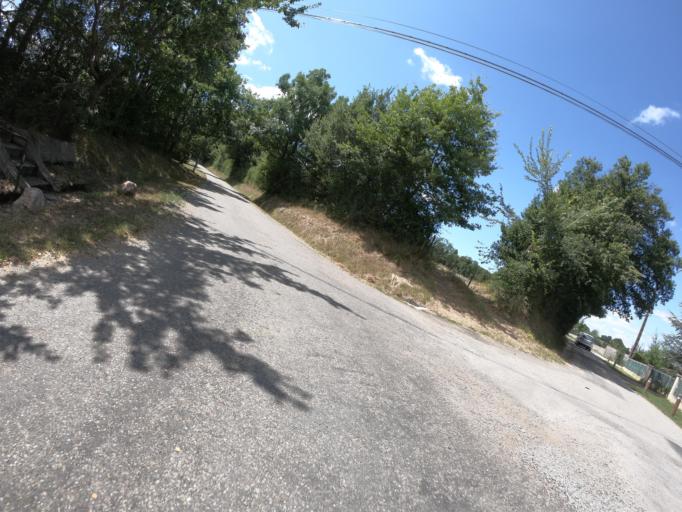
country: FR
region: Midi-Pyrenees
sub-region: Departement de l'Ariege
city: La Tour-du-Crieu
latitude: 43.0799
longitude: 1.7381
